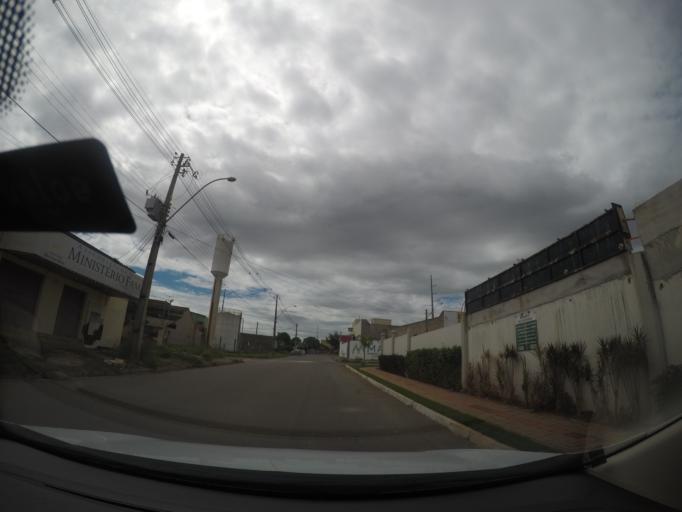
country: BR
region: Goias
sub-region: Goiania
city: Goiania
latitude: -16.7295
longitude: -49.3415
